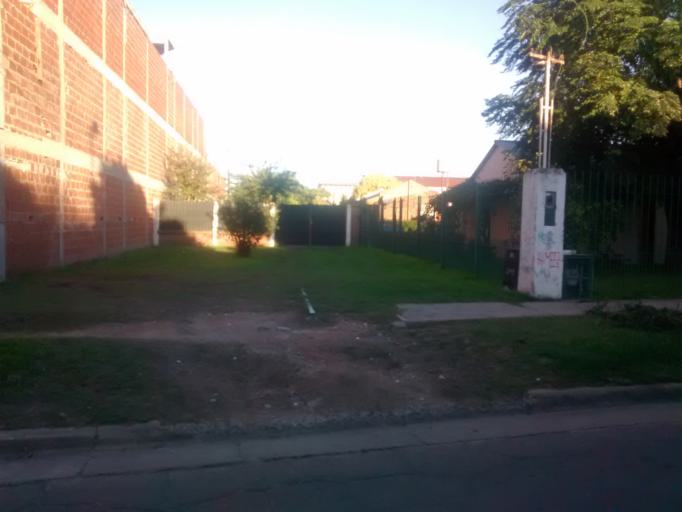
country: AR
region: Buenos Aires
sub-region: Partido de La Plata
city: La Plata
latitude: -34.9102
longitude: -57.9219
